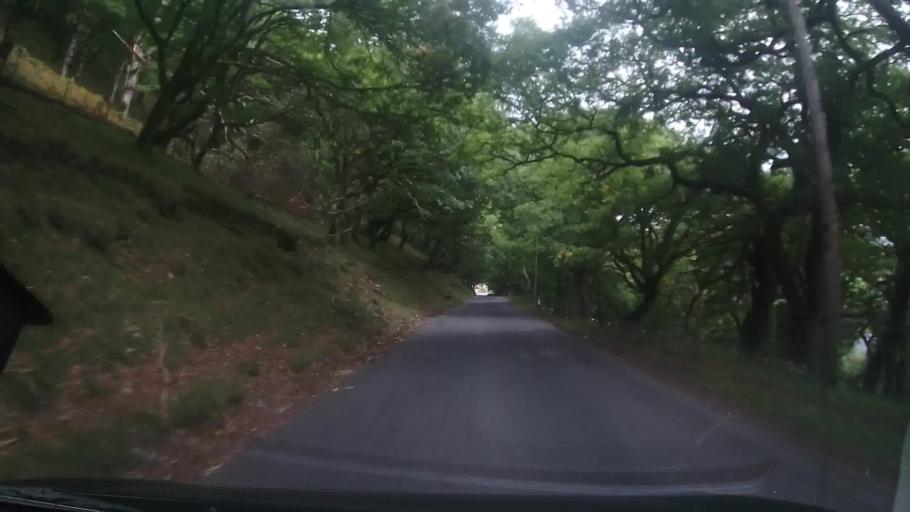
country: GB
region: Wales
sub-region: Sir Powys
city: Rhayader
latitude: 52.3122
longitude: -3.5454
